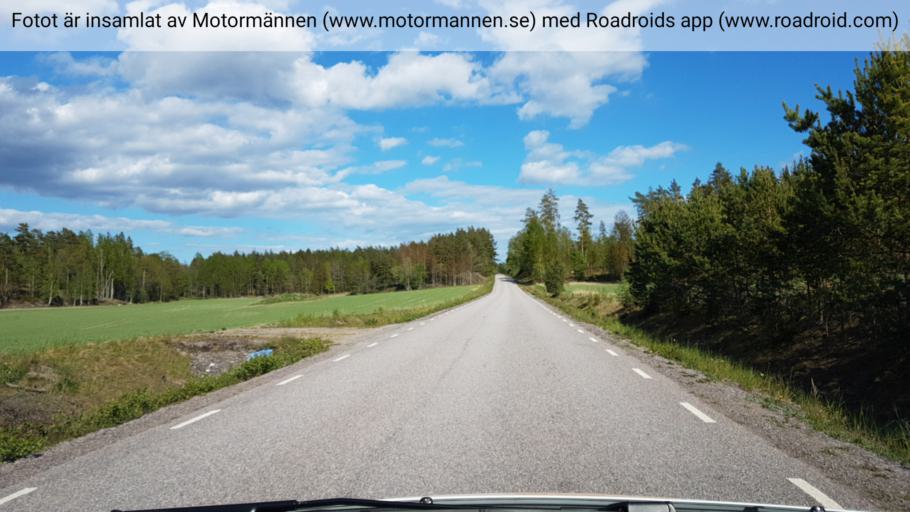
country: SE
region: Kalmar
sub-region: Vasterviks Kommun
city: Gamleby
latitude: 57.9215
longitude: 16.4310
